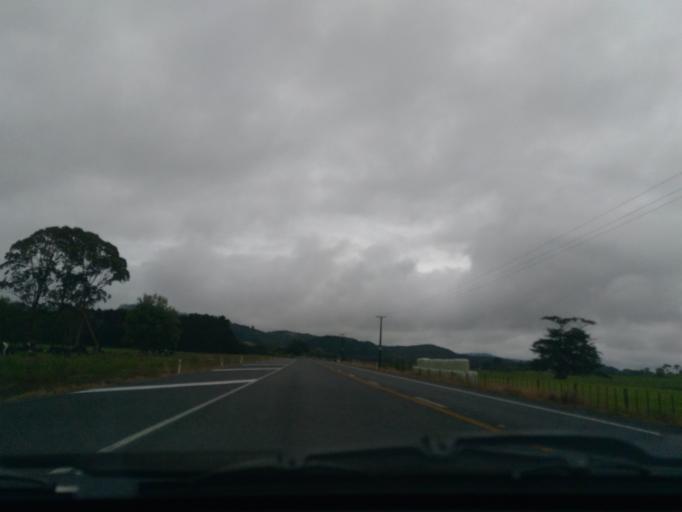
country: NZ
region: Northland
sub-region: Whangarei
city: Ruakaka
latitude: -36.0080
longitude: 174.4167
